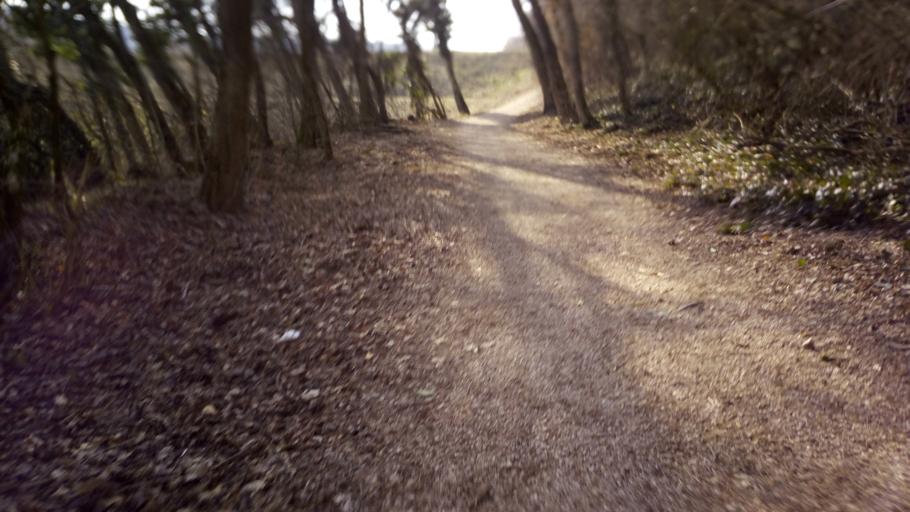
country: HU
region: Baranya
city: Pellerd
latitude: 46.0090
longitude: 18.1997
